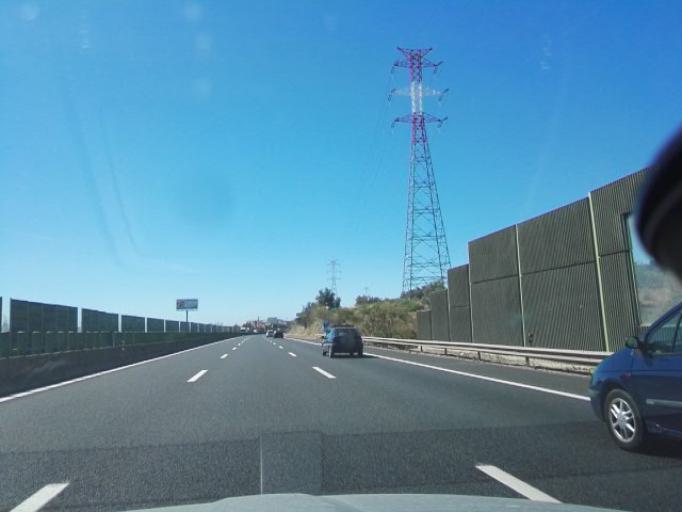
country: PT
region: Lisbon
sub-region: Loures
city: Santa Iria da Azoia
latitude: 38.8587
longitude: -9.0827
